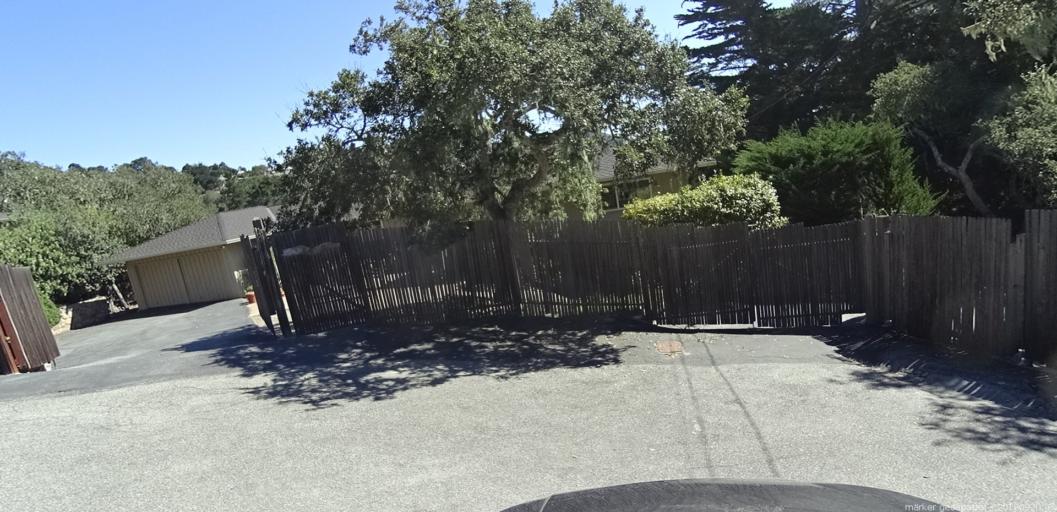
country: US
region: California
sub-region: Monterey County
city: Carmel-by-the-Sea
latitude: 36.5589
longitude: -121.9102
